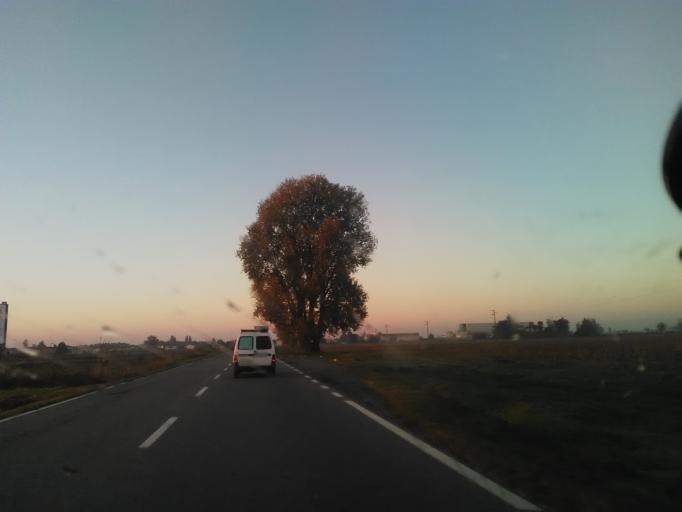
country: IT
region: Piedmont
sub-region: Provincia di Vercelli
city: Tronzano Vercellese
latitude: 45.3513
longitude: 8.1690
